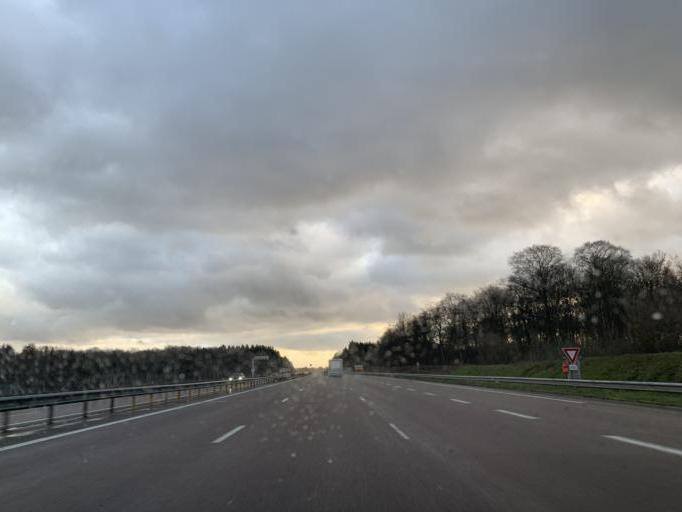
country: FR
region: Champagne-Ardenne
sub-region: Departement de la Haute-Marne
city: Langres
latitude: 47.8111
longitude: 5.2237
